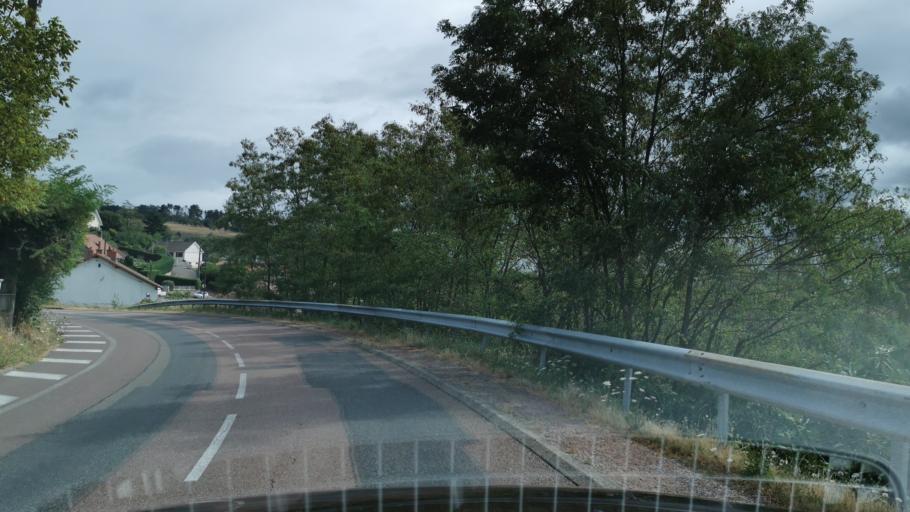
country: FR
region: Bourgogne
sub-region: Departement de Saone-et-Loire
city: Montcenis
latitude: 46.7974
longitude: 4.3960
